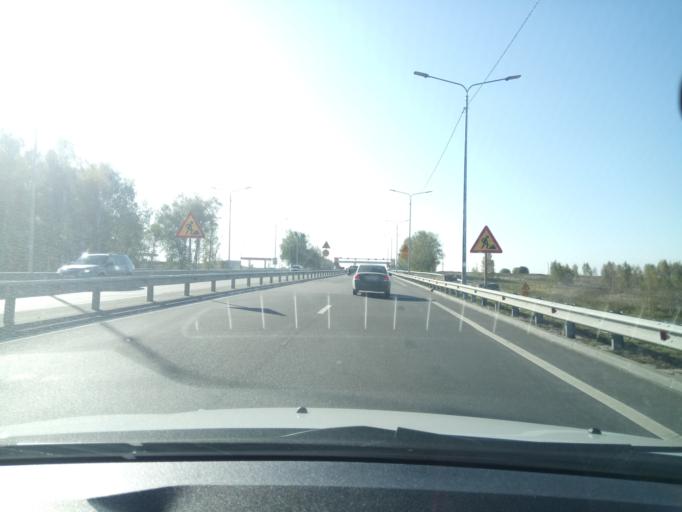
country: RU
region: Nizjnij Novgorod
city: Burevestnik
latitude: 56.0030
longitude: 43.9666
